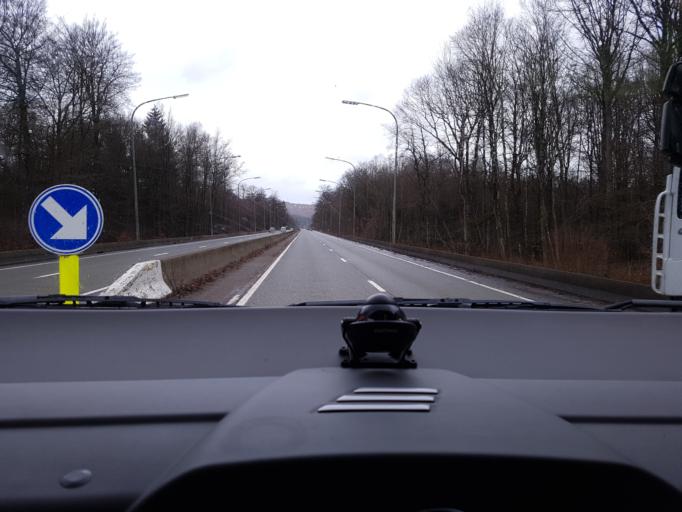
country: BE
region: Wallonia
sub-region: Province du Luxembourg
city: Tenneville
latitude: 50.1122
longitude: 5.4697
